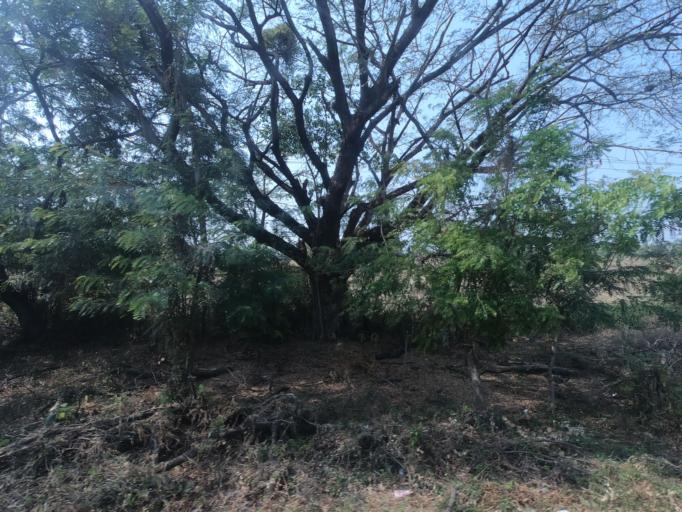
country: TH
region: Nakhon Ratchasima
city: Non Daeng
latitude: 15.3647
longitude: 102.4541
